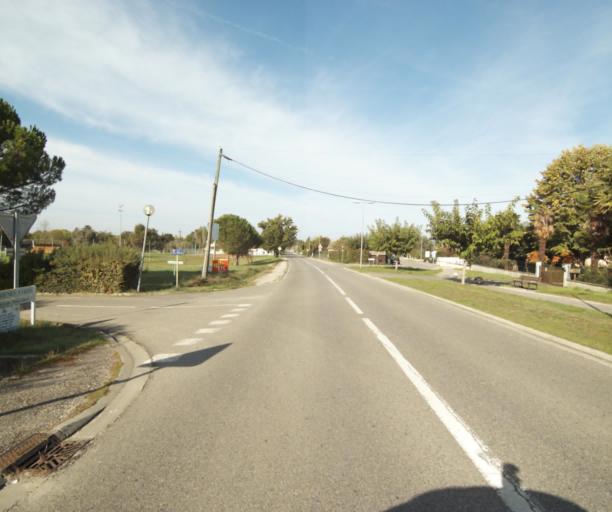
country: FR
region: Midi-Pyrenees
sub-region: Departement du Tarn-et-Garonne
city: Nohic
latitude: 43.9084
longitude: 1.4491
